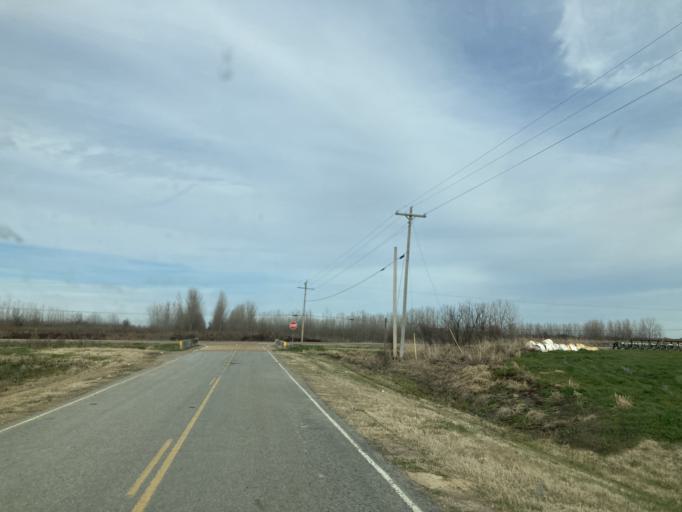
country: US
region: Mississippi
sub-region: Humphreys County
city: Belzoni
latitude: 33.1825
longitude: -90.6065
